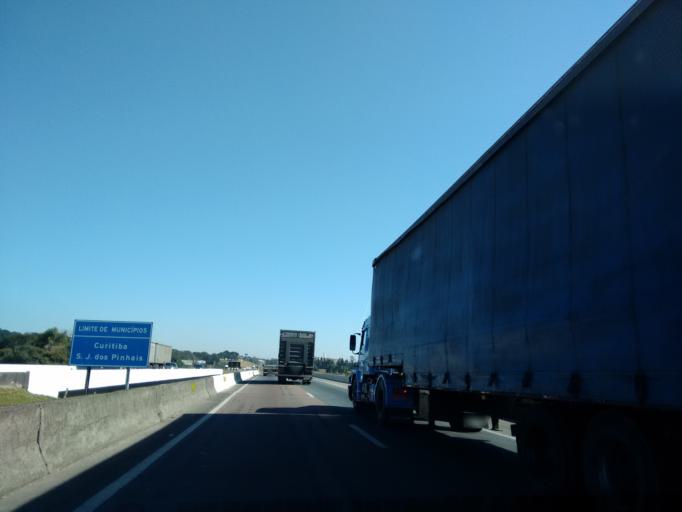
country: BR
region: Parana
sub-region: Sao Jose Dos Pinhais
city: Sao Jose dos Pinhais
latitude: -25.5669
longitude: -49.2391
